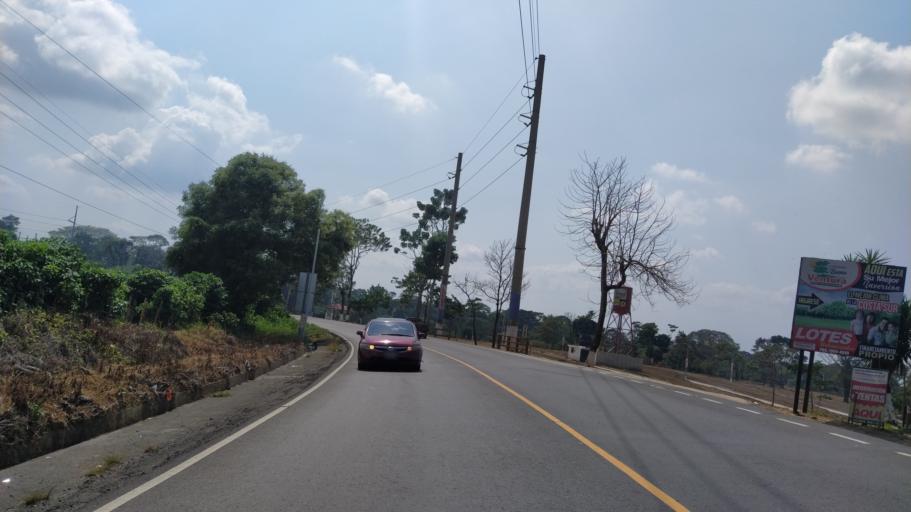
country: GT
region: Retalhuleu
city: San Felipe
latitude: 14.6296
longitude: -91.5863
